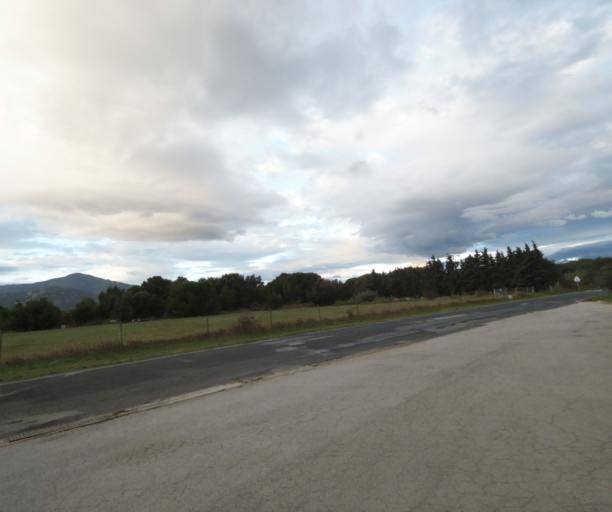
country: FR
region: Languedoc-Roussillon
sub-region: Departement des Pyrenees-Orientales
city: Argelers
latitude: 42.5633
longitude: 3.0111
